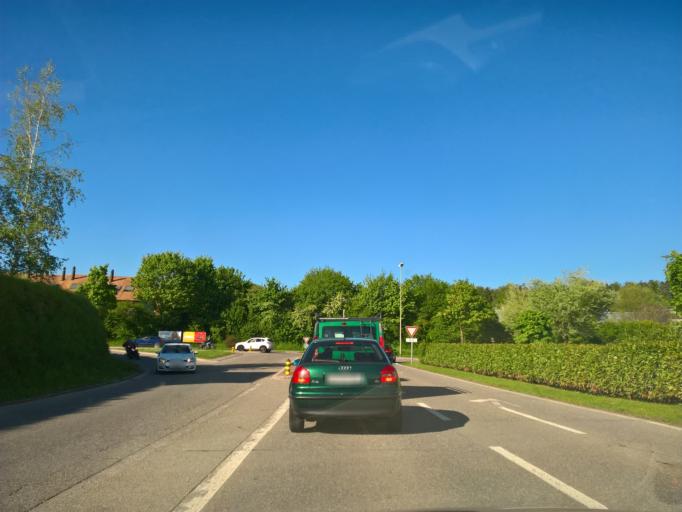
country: CH
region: Zurich
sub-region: Bezirk Buelach
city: Bassersdorf
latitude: 47.4397
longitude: 8.6336
